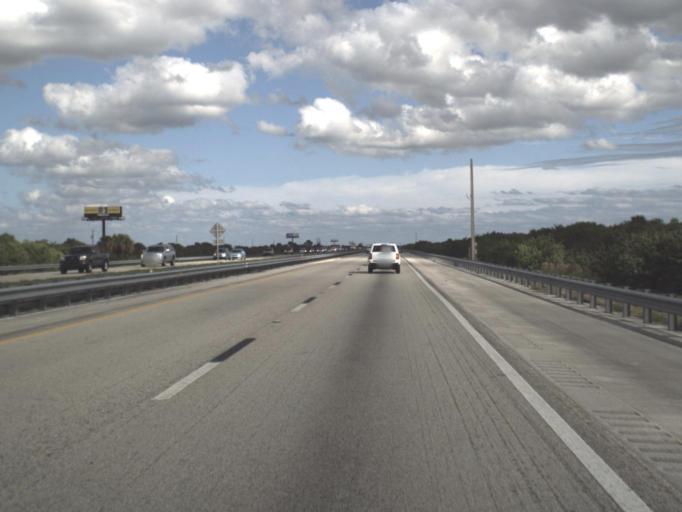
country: US
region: Florida
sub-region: Saint Lucie County
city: Lakewood Park
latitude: 27.4848
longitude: -80.5107
